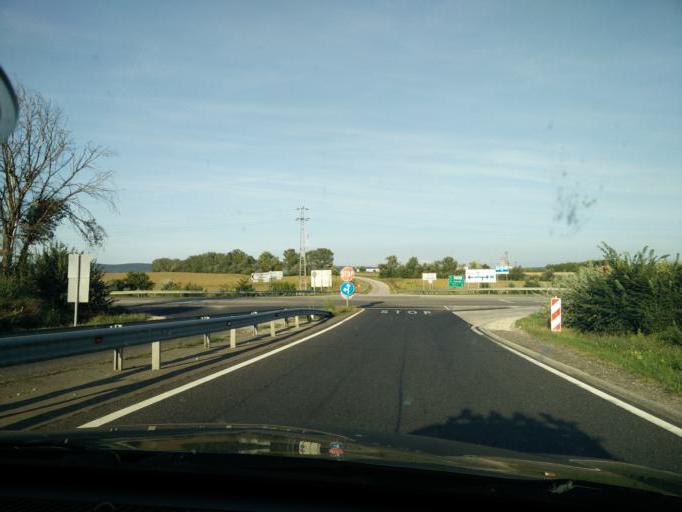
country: HU
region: Pest
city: Zsambek
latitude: 47.5093
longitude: 18.7589
